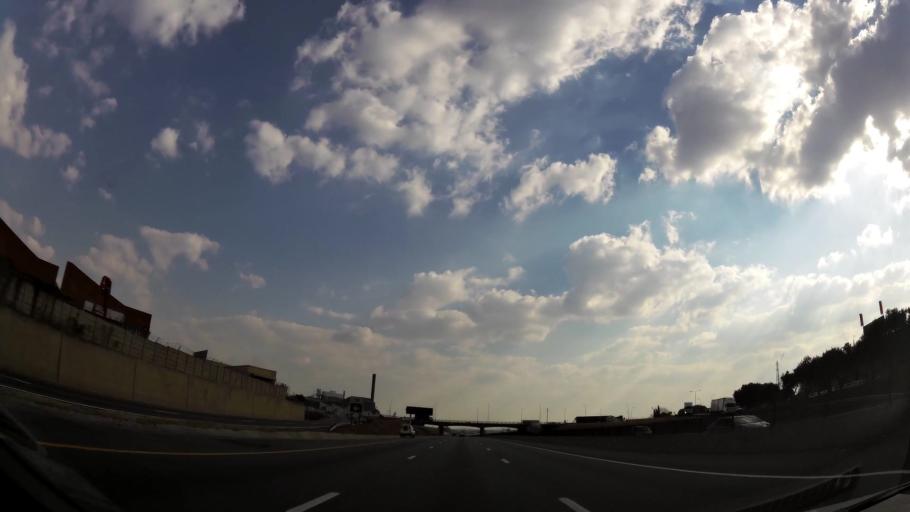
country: ZA
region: Gauteng
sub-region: Ekurhuleni Metropolitan Municipality
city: Germiston
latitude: -26.2552
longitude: 28.1907
